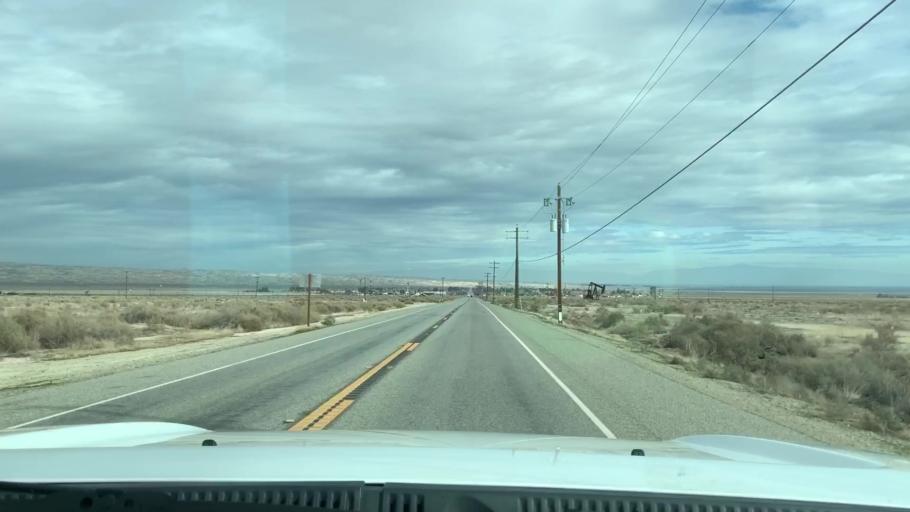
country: US
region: California
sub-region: Kern County
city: Ford City
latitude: 35.1942
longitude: -119.4281
